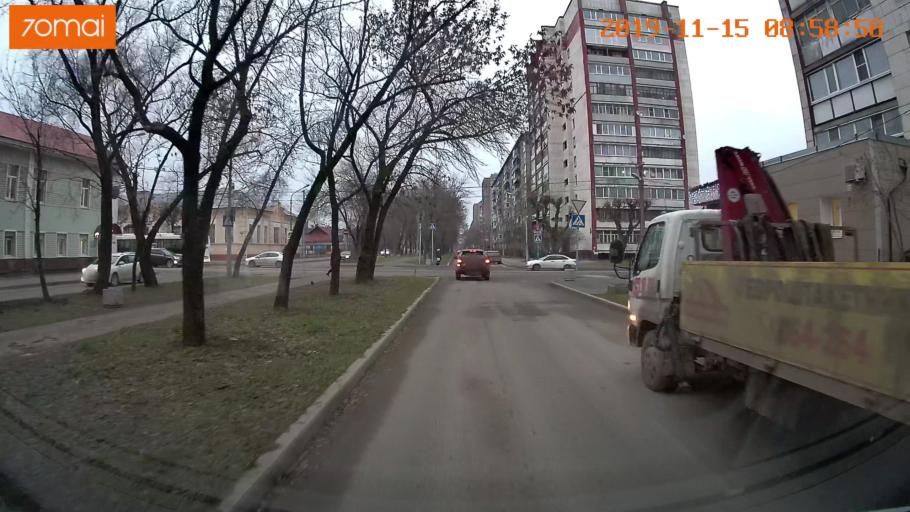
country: RU
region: Vologda
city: Cherepovets
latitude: 59.1276
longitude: 37.9238
